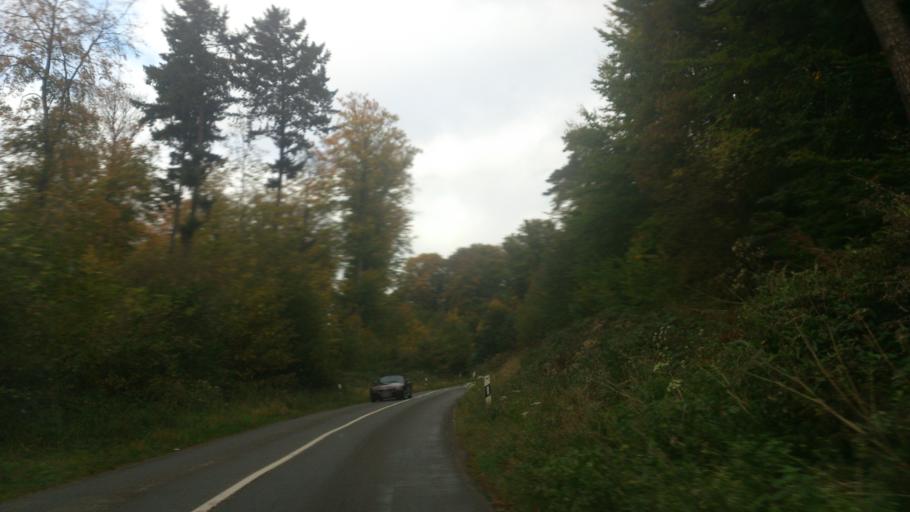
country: DE
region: Baden-Wuerttemberg
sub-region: Karlsruhe Region
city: Heidelberg
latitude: 49.3823
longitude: 8.7033
